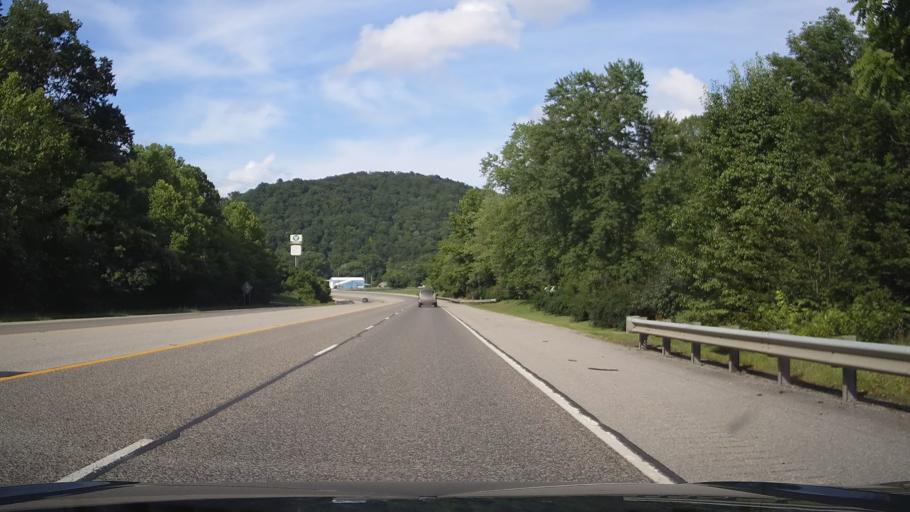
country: US
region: Kentucky
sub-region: Lawrence County
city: Louisa
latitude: 37.9907
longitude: -82.6621
